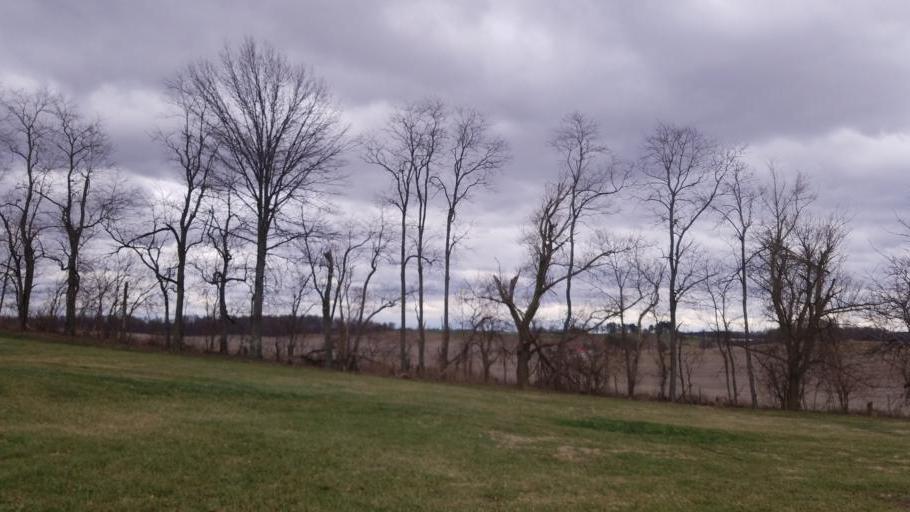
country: US
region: Ohio
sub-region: Licking County
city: Utica
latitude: 40.2295
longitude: -82.4072
